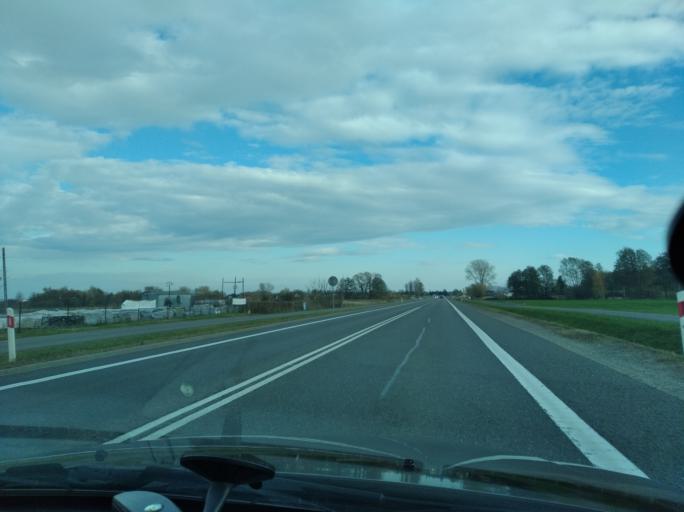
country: PL
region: Subcarpathian Voivodeship
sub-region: Powiat debicki
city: Debica
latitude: 50.0469
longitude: 21.4408
